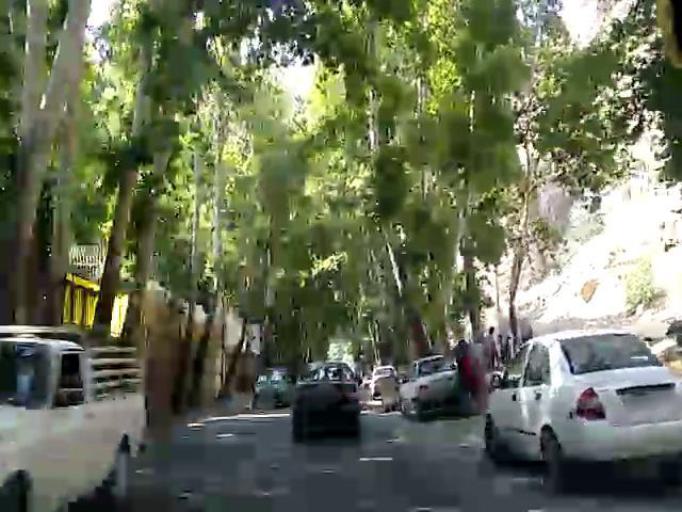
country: IR
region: Alborz
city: Karaj
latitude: 35.8929
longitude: 51.0460
